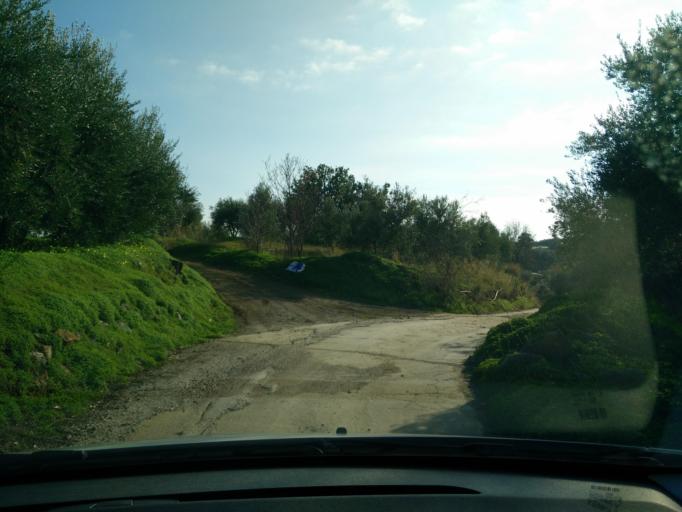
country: GR
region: Crete
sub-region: Nomos Lasithiou
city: Gra Liyia
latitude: 35.0284
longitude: 25.5693
